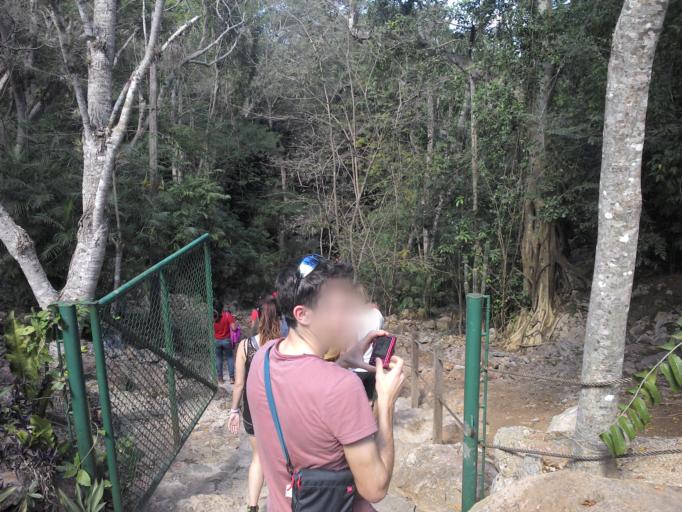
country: MX
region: Yucatan
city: Oxkutzkab
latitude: 20.2537
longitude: -89.4559
